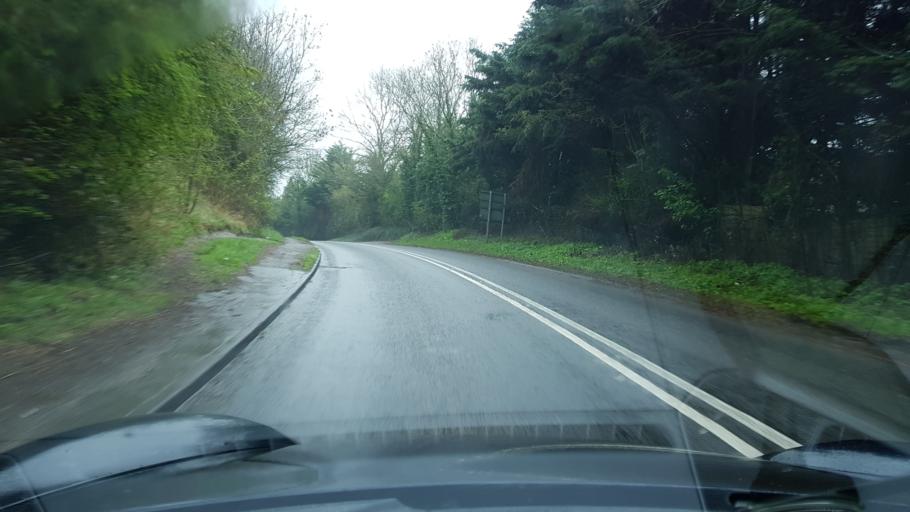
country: GB
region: England
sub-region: Gloucestershire
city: Mitcheldean
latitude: 51.8634
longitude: -2.4394
